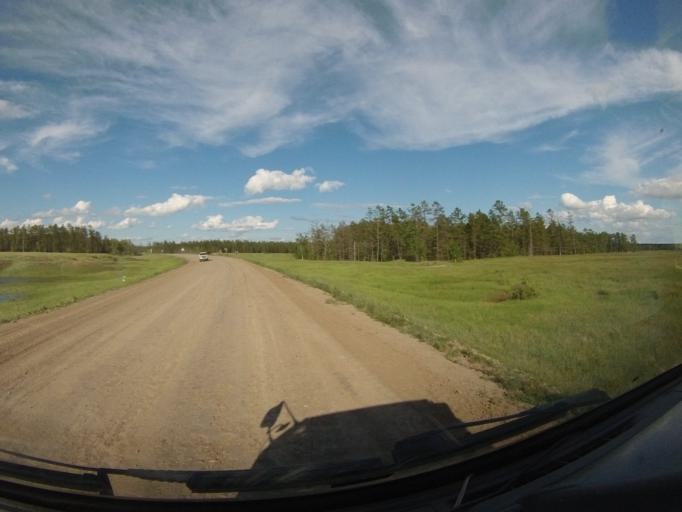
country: RU
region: Sakha
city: Ytyk-Kyuyel'
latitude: 62.2221
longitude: 133.2782
